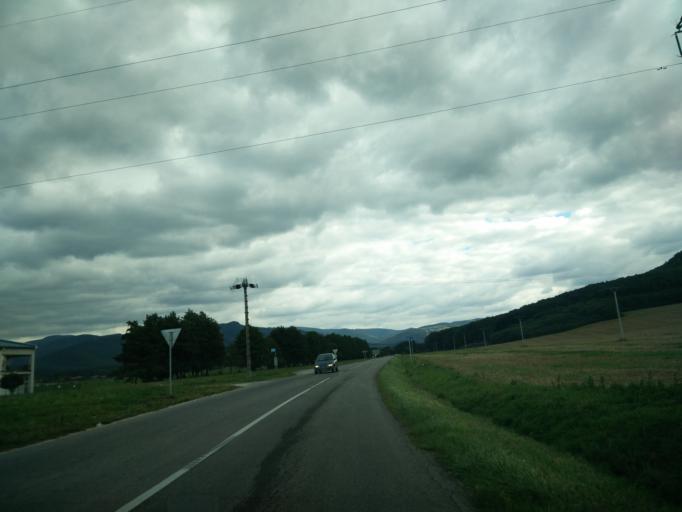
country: SK
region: Nitriansky
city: Partizanske
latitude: 48.6243
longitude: 18.4558
